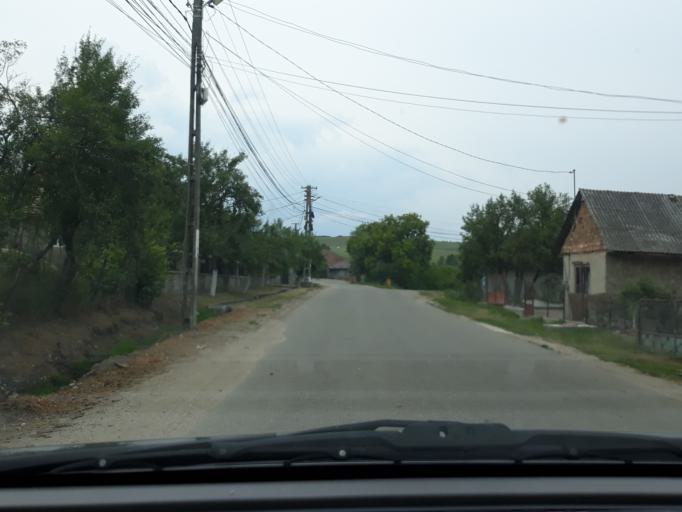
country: RO
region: Salaj
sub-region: Comuna Criseni
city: Criseni
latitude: 47.2540
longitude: 23.0648
